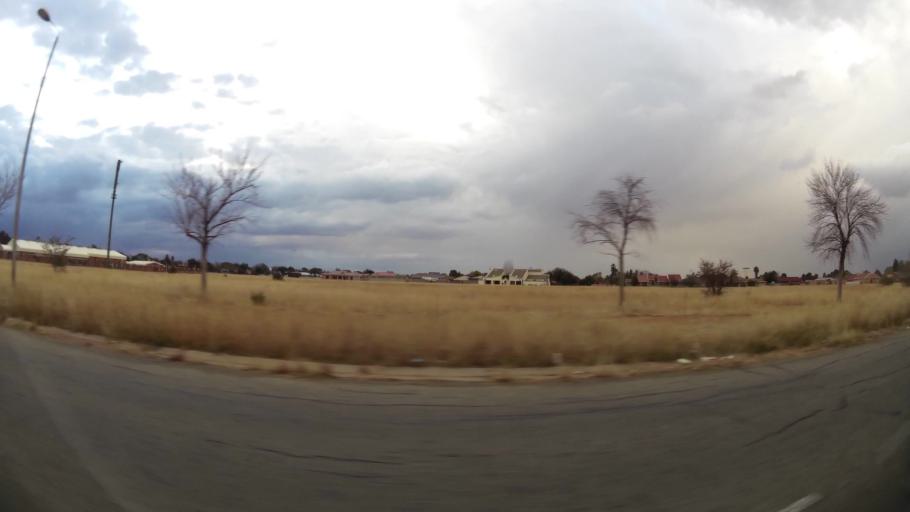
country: ZA
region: Orange Free State
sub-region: Lejweleputswa District Municipality
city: Welkom
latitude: -27.9548
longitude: 26.7373
